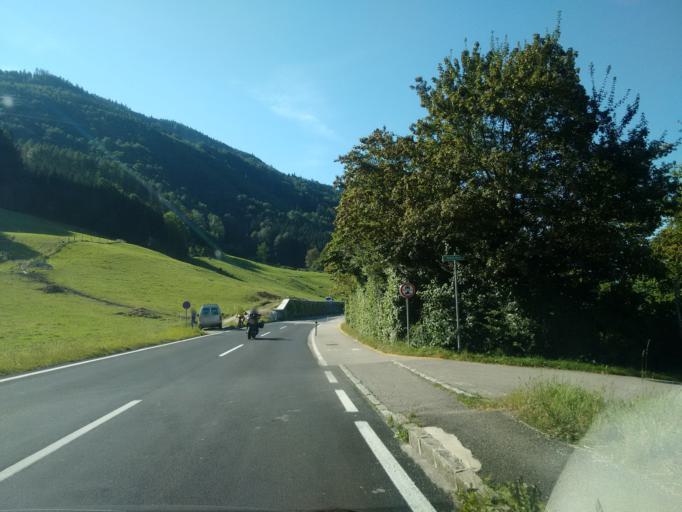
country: AT
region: Upper Austria
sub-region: Politischer Bezirk Vocklabruck
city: Steinbach am Attersee
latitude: 47.8725
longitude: 13.5678
